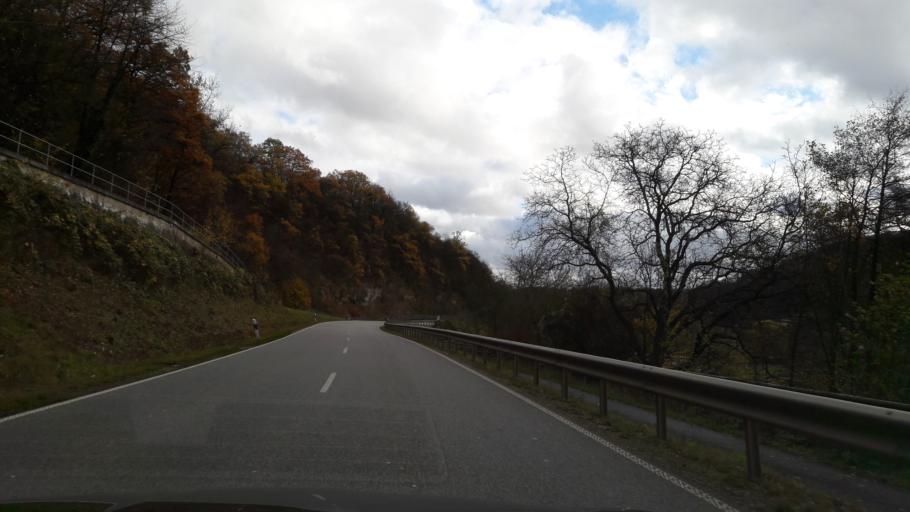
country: DE
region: Rheinland-Pfalz
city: Menningen
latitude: 49.8199
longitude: 6.4795
